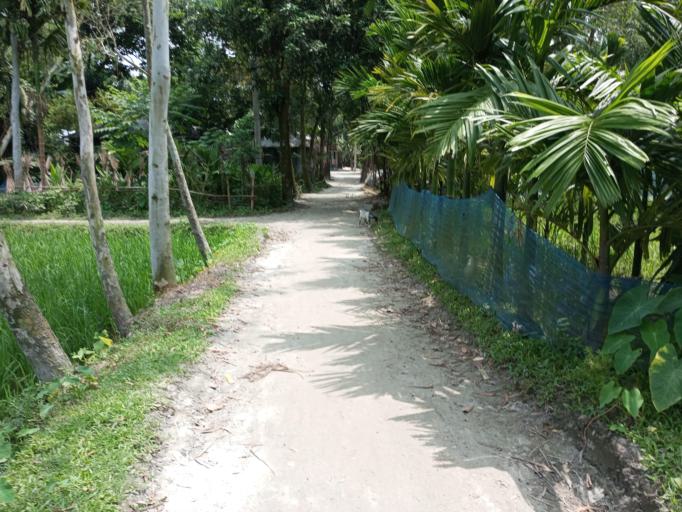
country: BD
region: Rangpur Division
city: Rangpur
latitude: 25.9063
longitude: 89.2690
